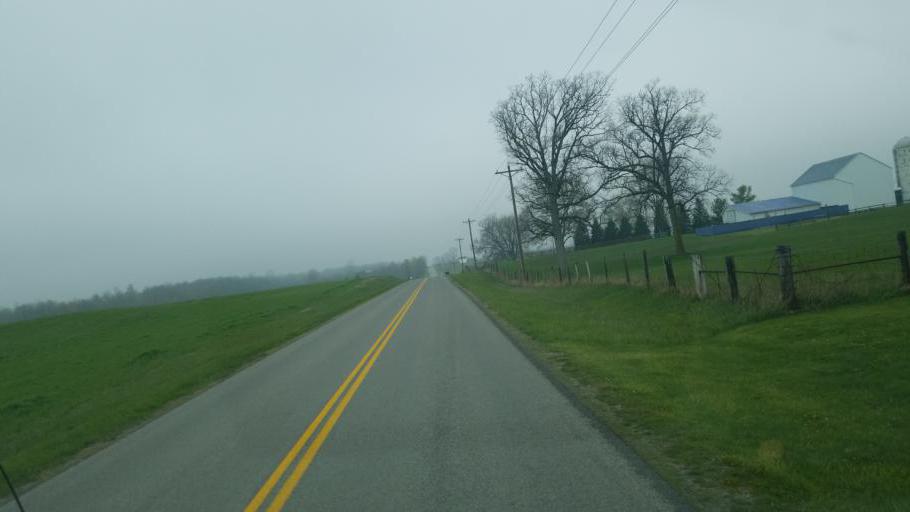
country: US
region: Ohio
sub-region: Logan County
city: Bellefontaine
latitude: 40.3872
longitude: -83.8216
